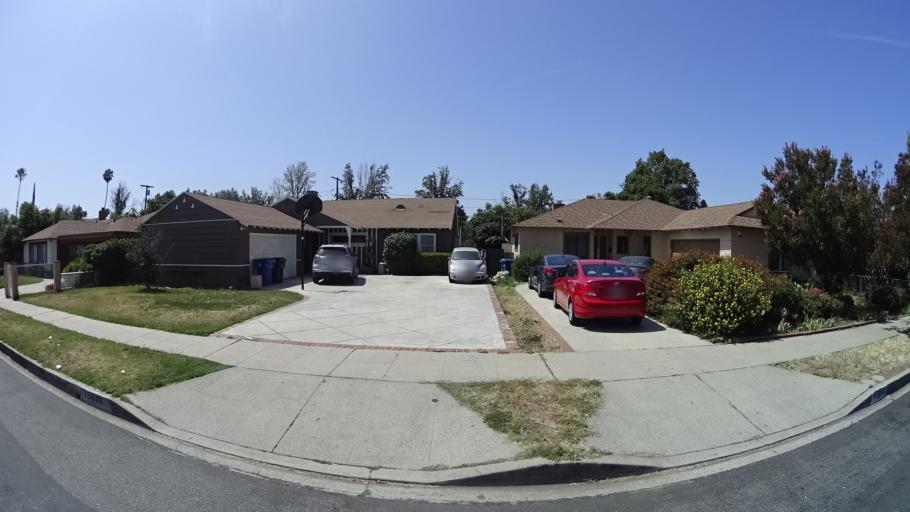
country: US
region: California
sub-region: Los Angeles County
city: Van Nuys
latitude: 34.2048
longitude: -118.4613
